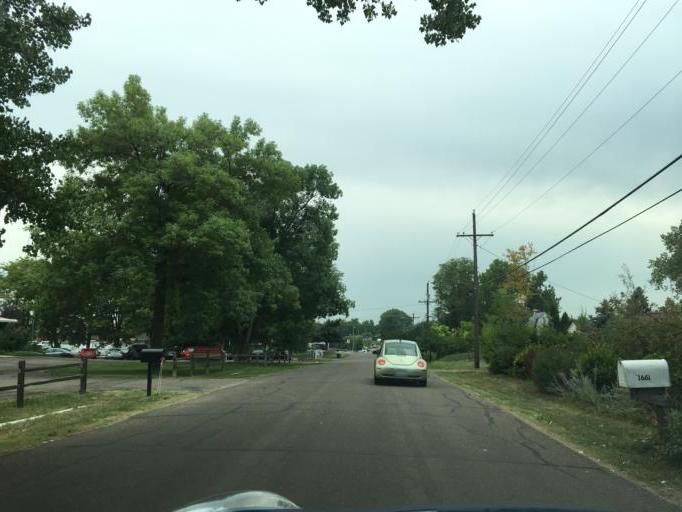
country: US
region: Colorado
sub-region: Jefferson County
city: Wheat Ridge
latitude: 39.7429
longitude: -105.1014
